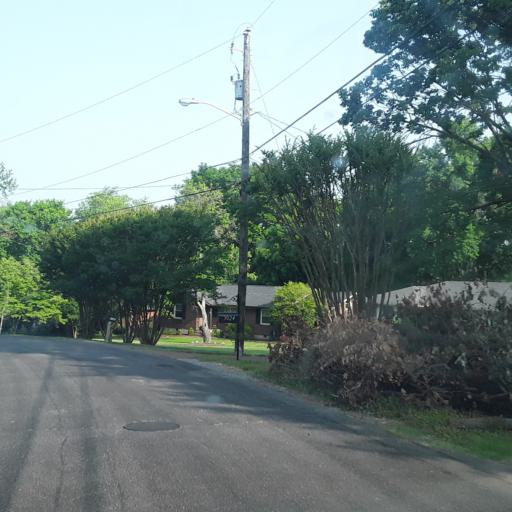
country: US
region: Tennessee
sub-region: Davidson County
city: Oak Hill
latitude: 36.0612
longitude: -86.7516
